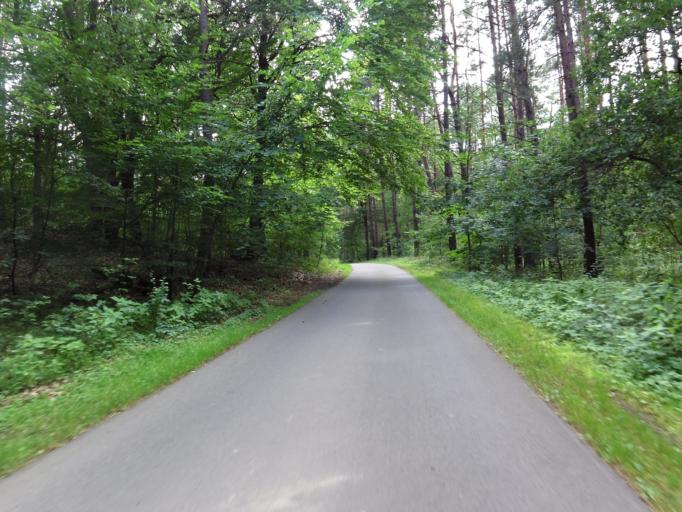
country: DE
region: Brandenburg
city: Lychen
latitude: 53.2301
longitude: 13.2765
